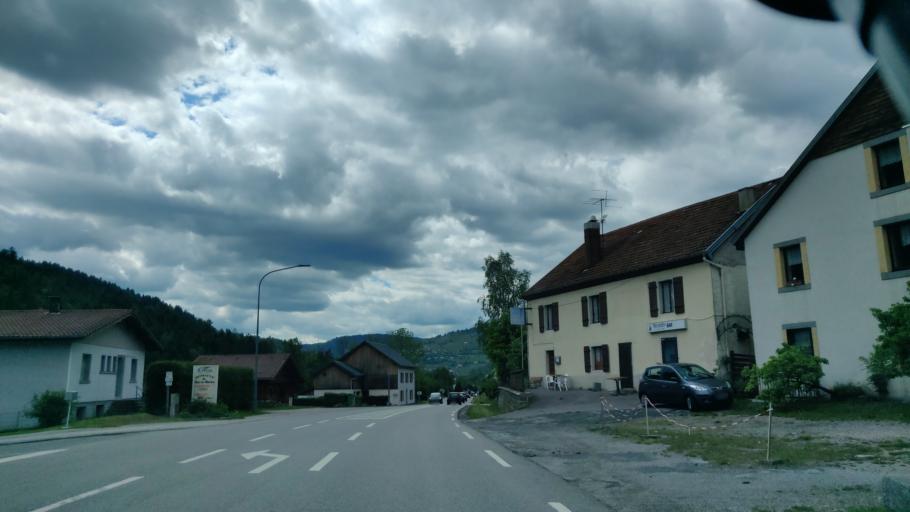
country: FR
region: Lorraine
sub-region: Departement des Vosges
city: La Bresse
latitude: 48.0015
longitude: 6.9153
